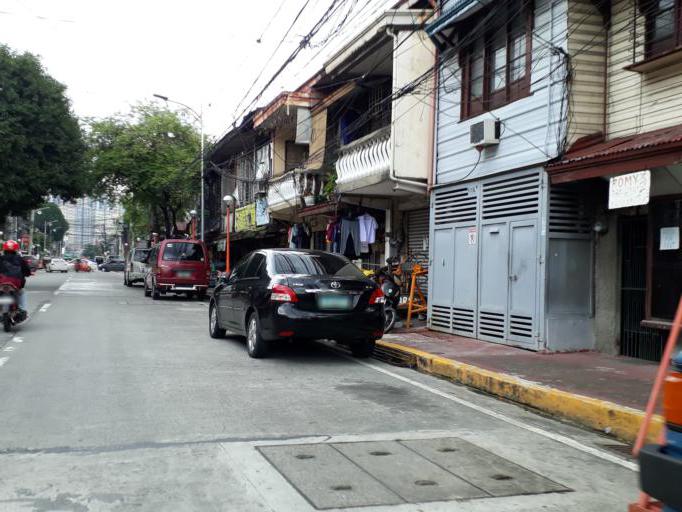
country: PH
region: Metro Manila
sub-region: City of Manila
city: Manila
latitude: 14.6138
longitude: 120.9920
